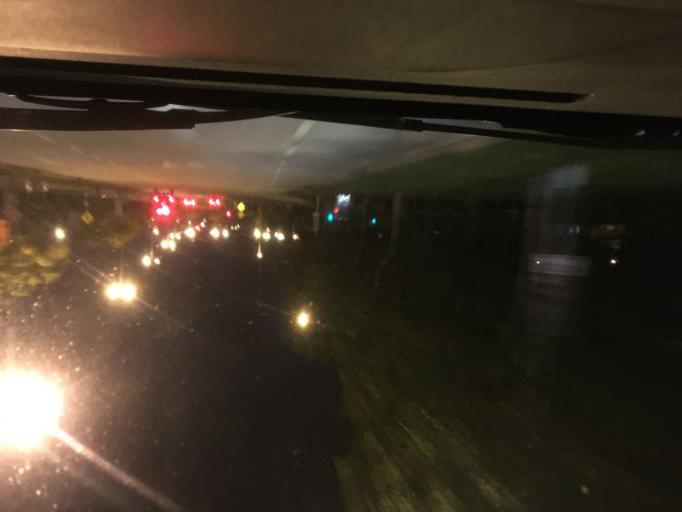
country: MY
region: Putrajaya
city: Putrajaya
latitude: 2.9114
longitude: 101.6545
